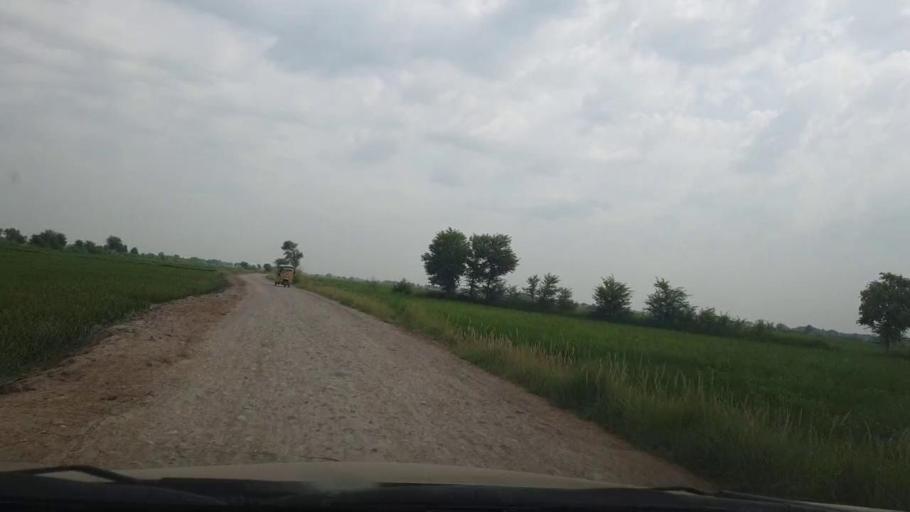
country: PK
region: Sindh
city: Ratodero
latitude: 27.7173
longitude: 68.2295
